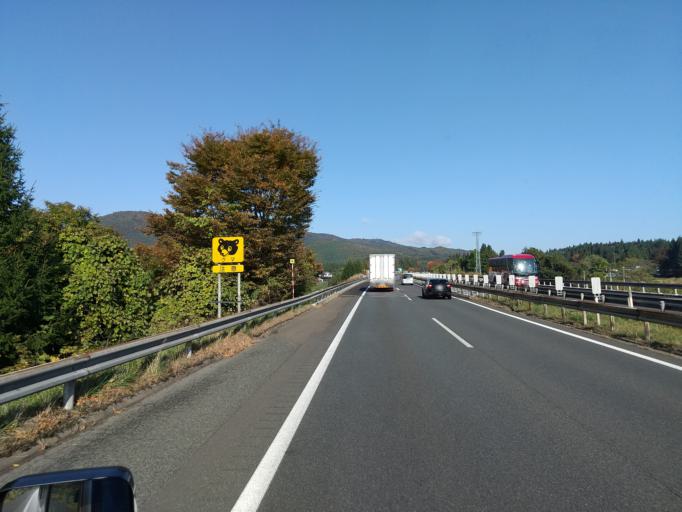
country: JP
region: Iwate
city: Hanamaki
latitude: 39.5003
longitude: 141.1043
